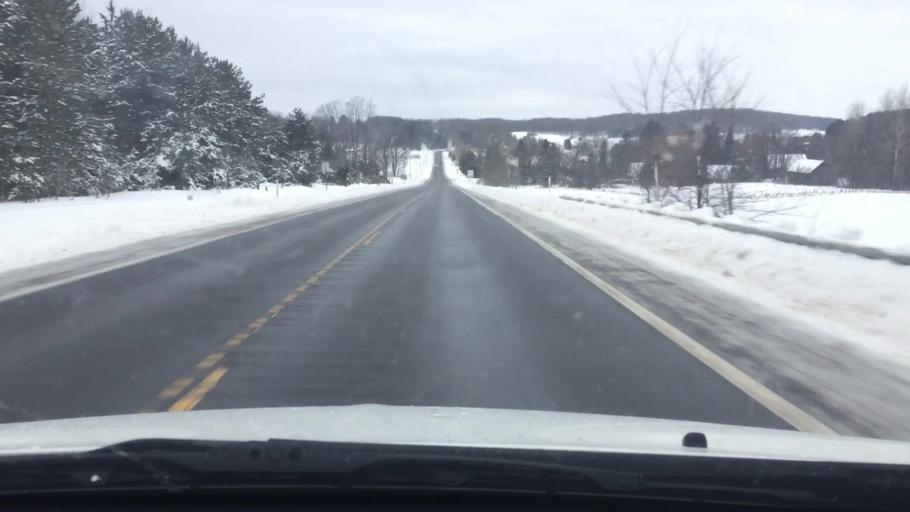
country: US
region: Michigan
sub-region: Charlevoix County
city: East Jordan
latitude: 45.1035
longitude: -85.0356
